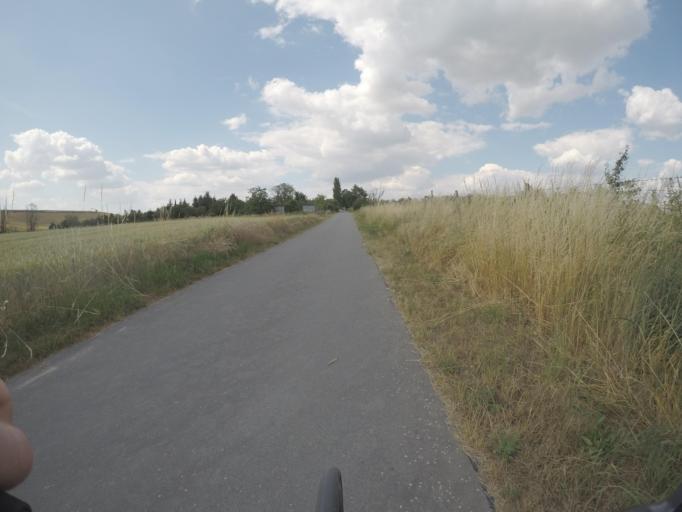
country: DE
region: Brandenburg
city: Ketzin
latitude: 52.4577
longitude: 12.7985
